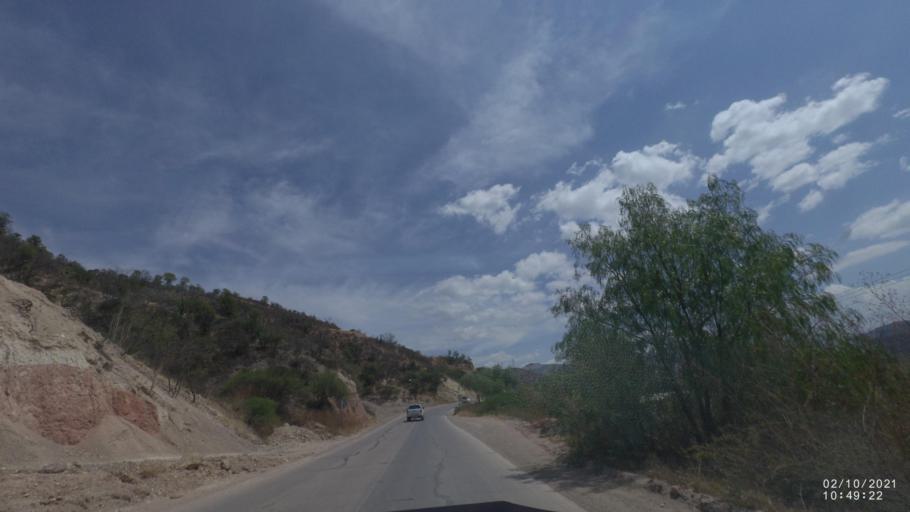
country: BO
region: Cochabamba
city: Sipe Sipe
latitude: -17.5808
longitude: -66.3441
